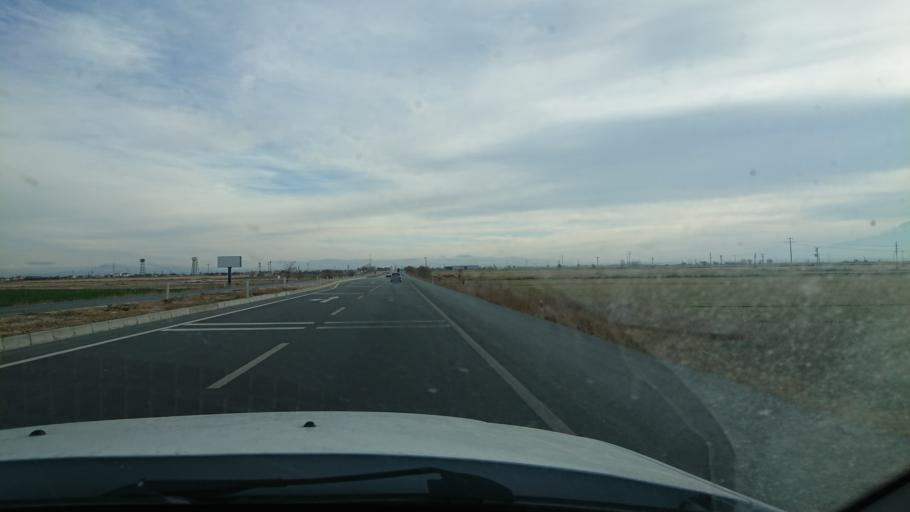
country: TR
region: Aksaray
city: Yesilova
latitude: 38.2868
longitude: 33.7416
